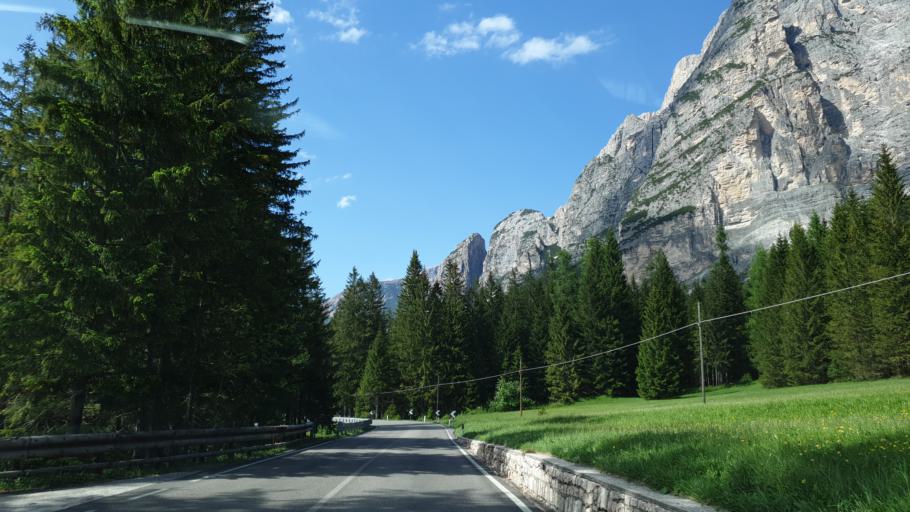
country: IT
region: Veneto
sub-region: Provincia di Belluno
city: Cortina d'Ampezzo
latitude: 46.5659
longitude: 12.1214
